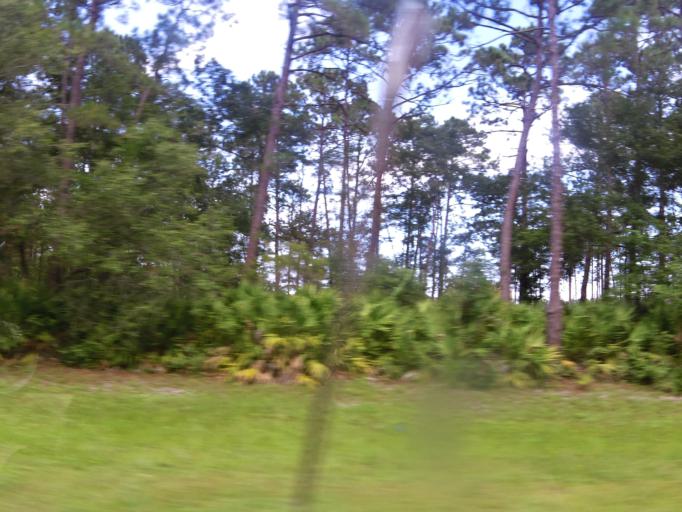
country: US
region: Florida
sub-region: Nassau County
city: Fernandina Beach
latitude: 30.6285
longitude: -81.4692
